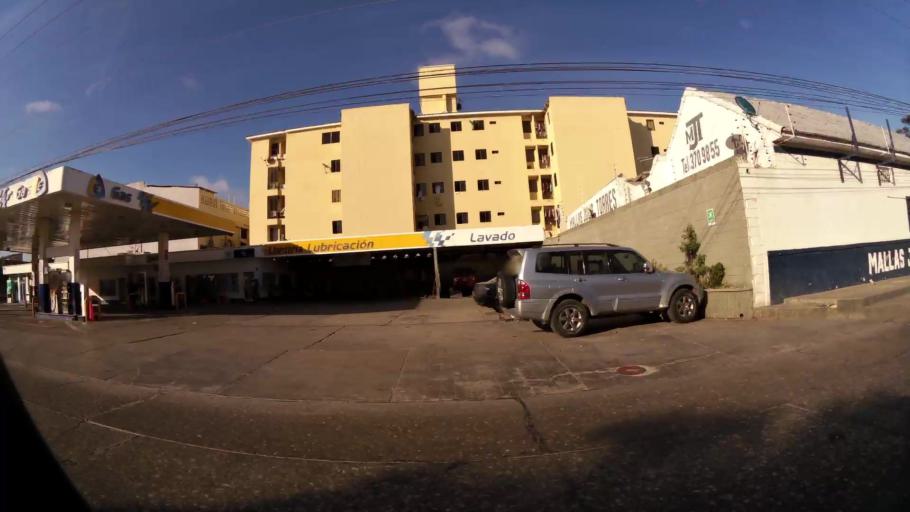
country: CO
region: Atlantico
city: Barranquilla
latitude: 10.9854
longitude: -74.7952
